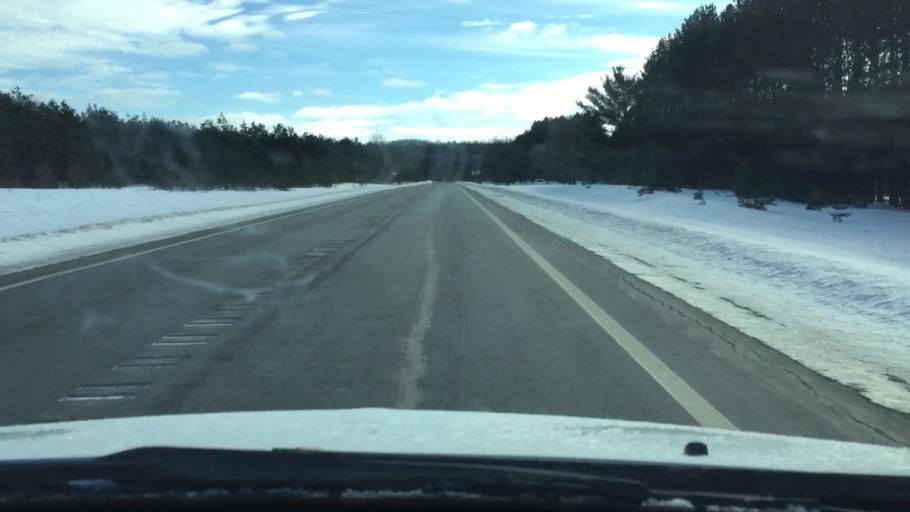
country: US
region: Michigan
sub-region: Antrim County
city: Mancelona
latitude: 44.9631
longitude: -85.0521
